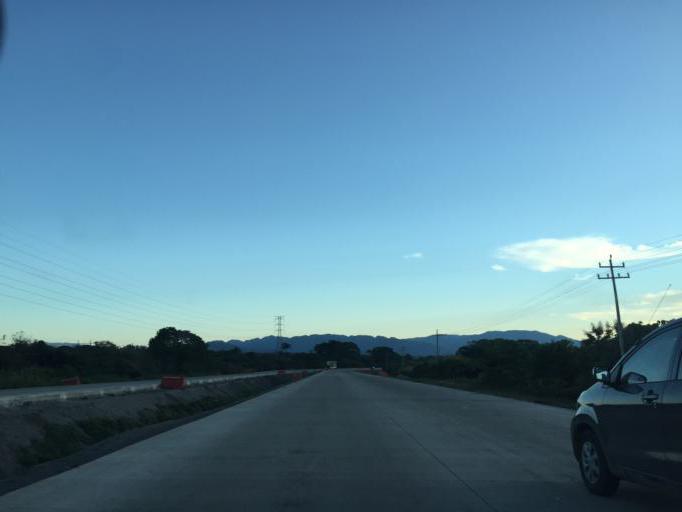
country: MX
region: Veracruz
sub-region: Ixtaczoquitlan
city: Buenavista
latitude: 18.9022
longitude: -97.0343
